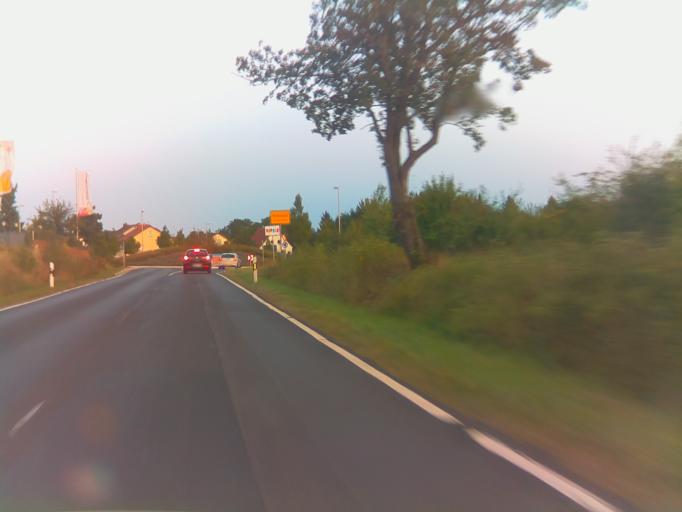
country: DE
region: Bavaria
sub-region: Regierungsbezirk Unterfranken
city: Oerlenbach
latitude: 50.1459
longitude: 10.1307
